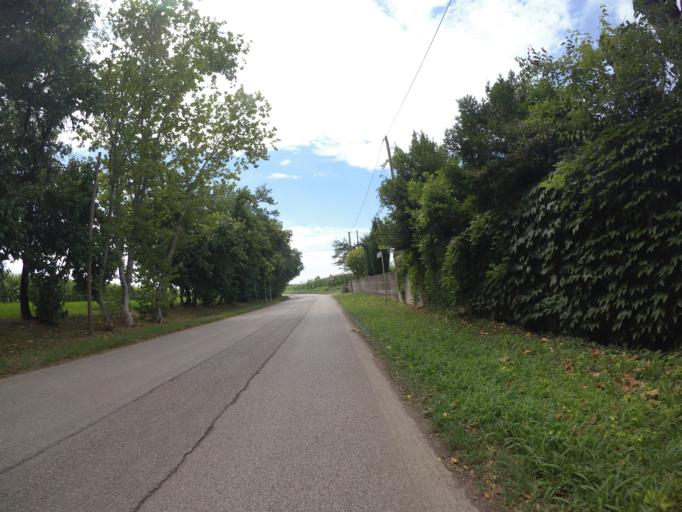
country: IT
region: Friuli Venezia Giulia
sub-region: Provincia di Udine
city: Basiliano
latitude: 45.9794
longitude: 13.0874
